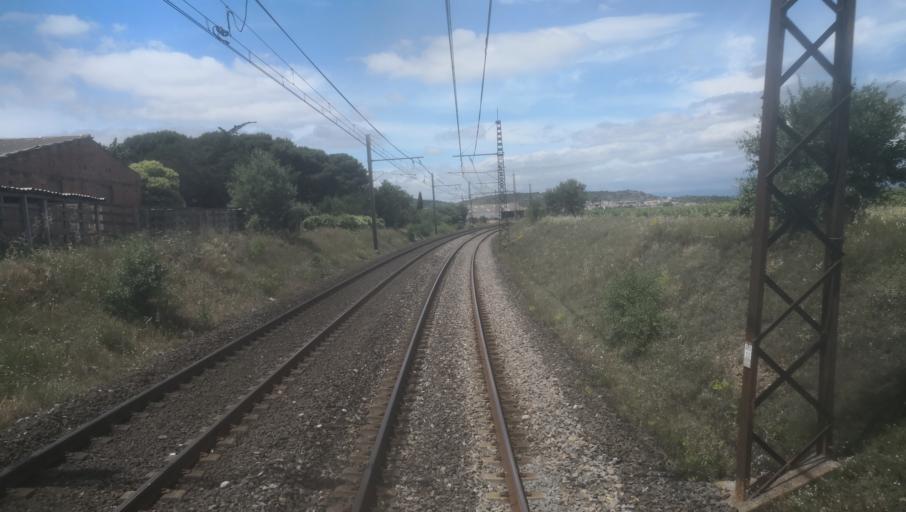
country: FR
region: Languedoc-Roussillon
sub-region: Departement de l'Aude
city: Marcorignan
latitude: 43.1838
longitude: 2.9430
